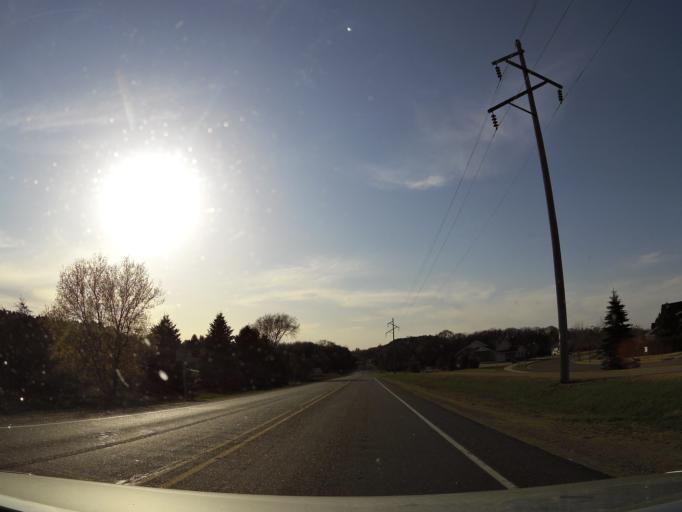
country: US
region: Wisconsin
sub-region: Pierce County
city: River Falls
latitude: 44.8303
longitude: -92.6314
